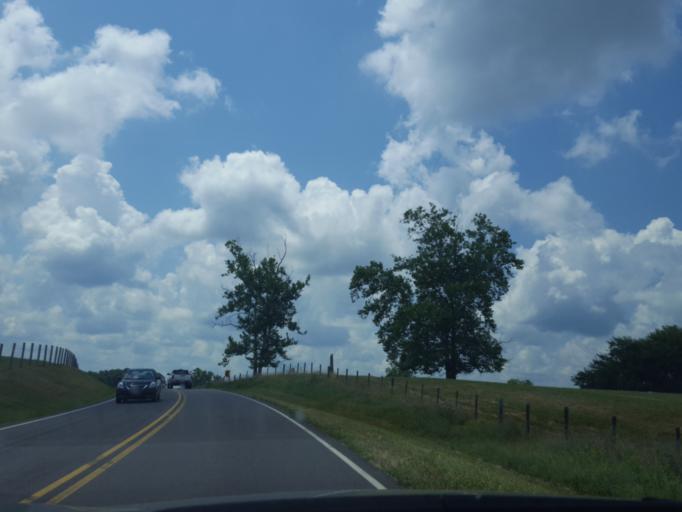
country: US
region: Virginia
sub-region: Orange County
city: Gordonsville
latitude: 38.1090
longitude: -78.2517
